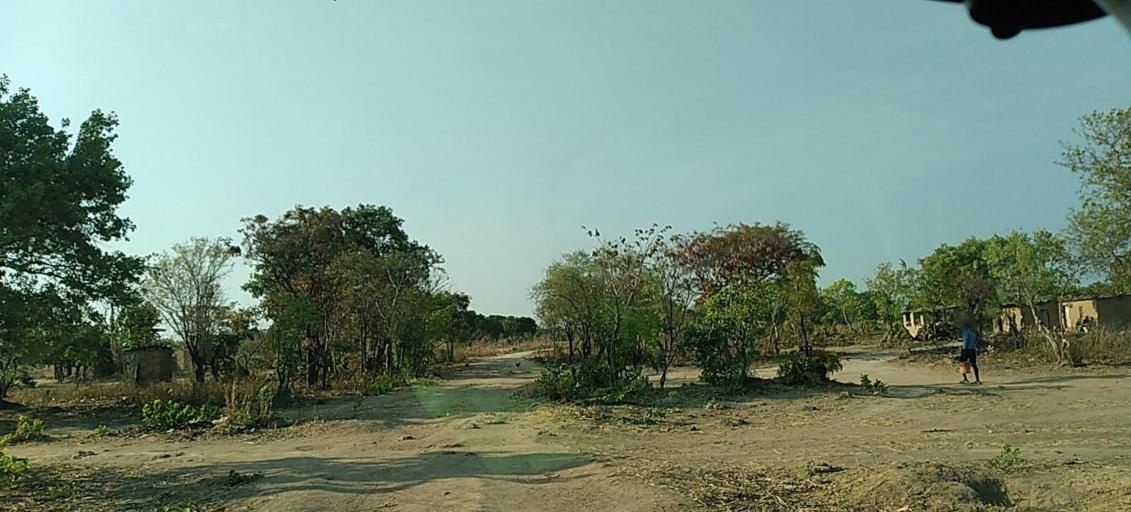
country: ZM
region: North-Western
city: Kalengwa
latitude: -13.1478
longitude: 25.0338
